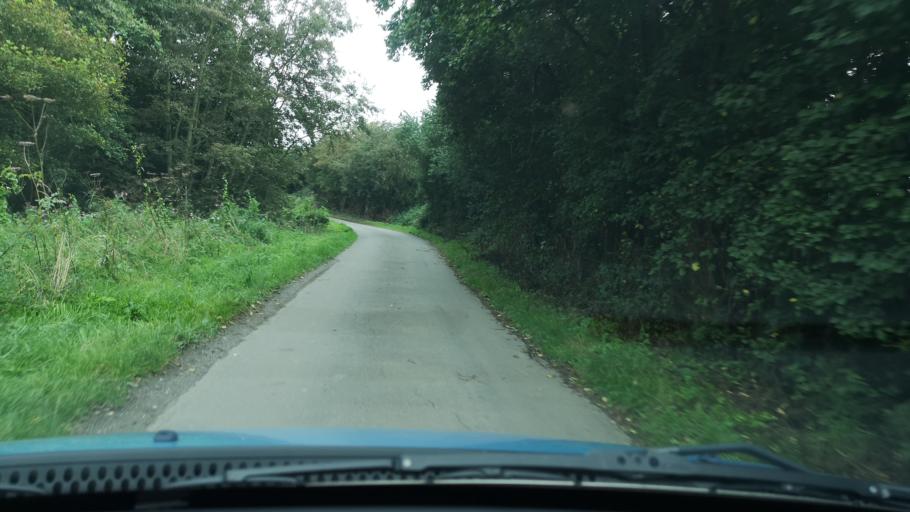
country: GB
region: England
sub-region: City and Borough of Wakefield
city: Featherstone
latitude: 53.6500
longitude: -1.3524
